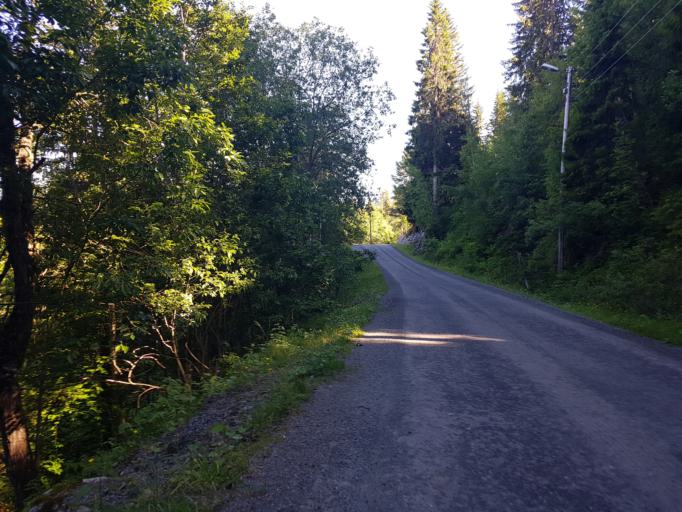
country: NO
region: Sor-Trondelag
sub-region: Trondheim
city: Trondheim
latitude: 63.4311
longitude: 10.2760
